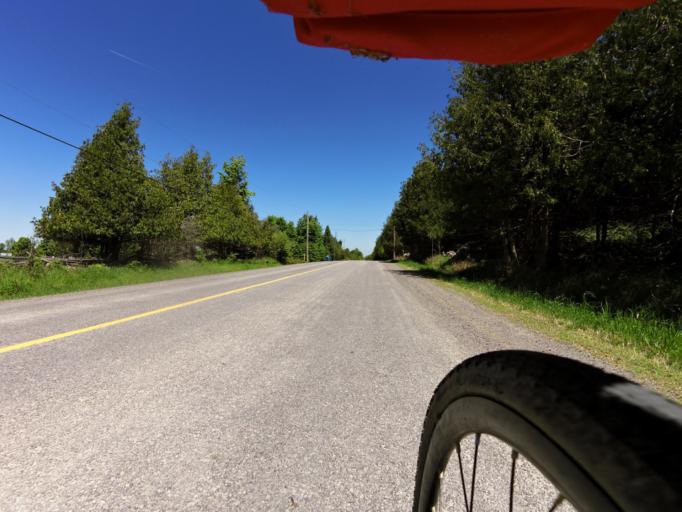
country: CA
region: Ontario
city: Carleton Place
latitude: 45.1631
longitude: -76.4273
